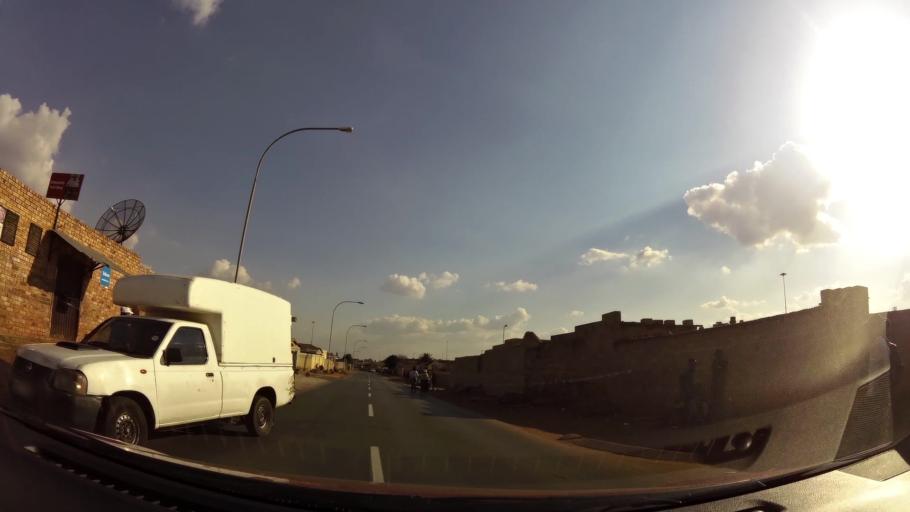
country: ZA
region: Gauteng
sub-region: City of Johannesburg Metropolitan Municipality
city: Soweto
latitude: -26.2307
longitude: 27.8689
